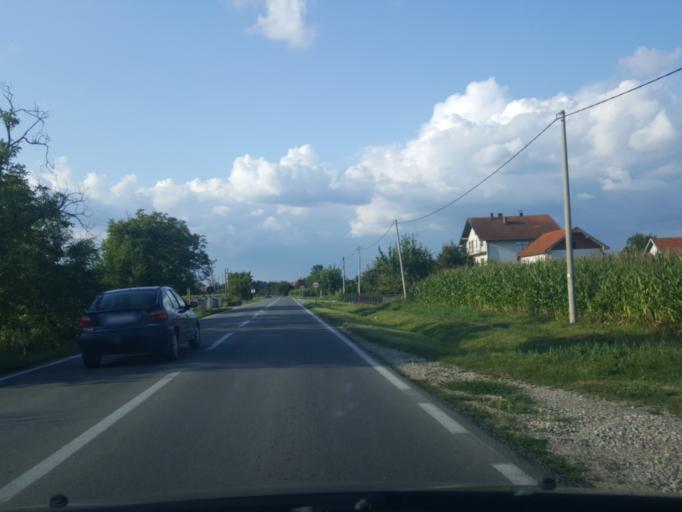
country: RS
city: Lipnicki Sor
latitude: 44.5889
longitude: 19.2581
